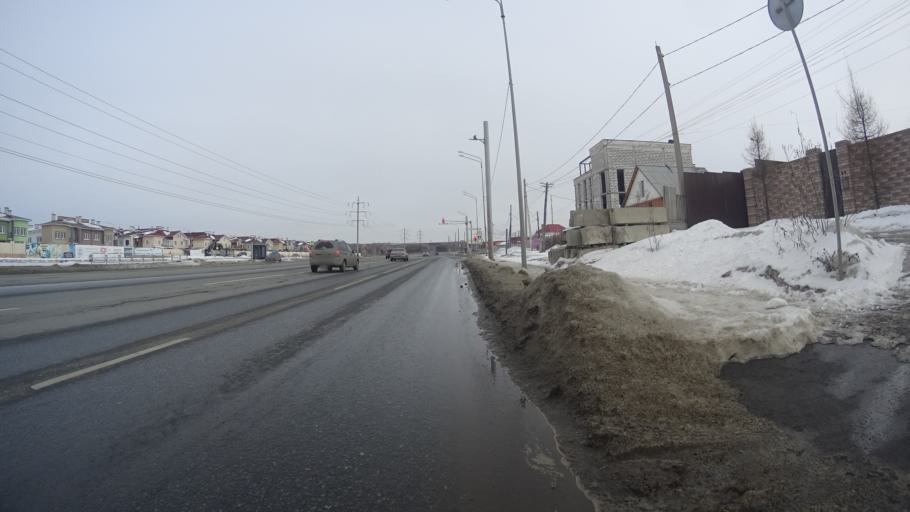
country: RU
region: Chelyabinsk
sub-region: Gorod Chelyabinsk
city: Chelyabinsk
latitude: 55.1555
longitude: 61.3121
